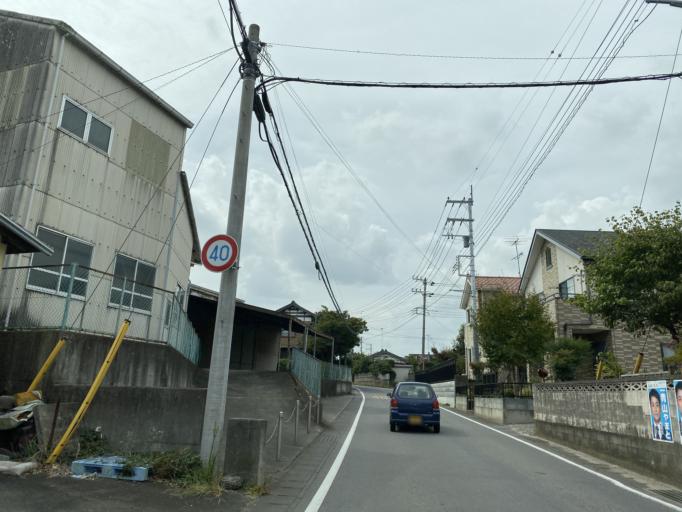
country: JP
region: Ibaraki
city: Mitsukaido
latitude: 36.0433
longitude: 140.0466
